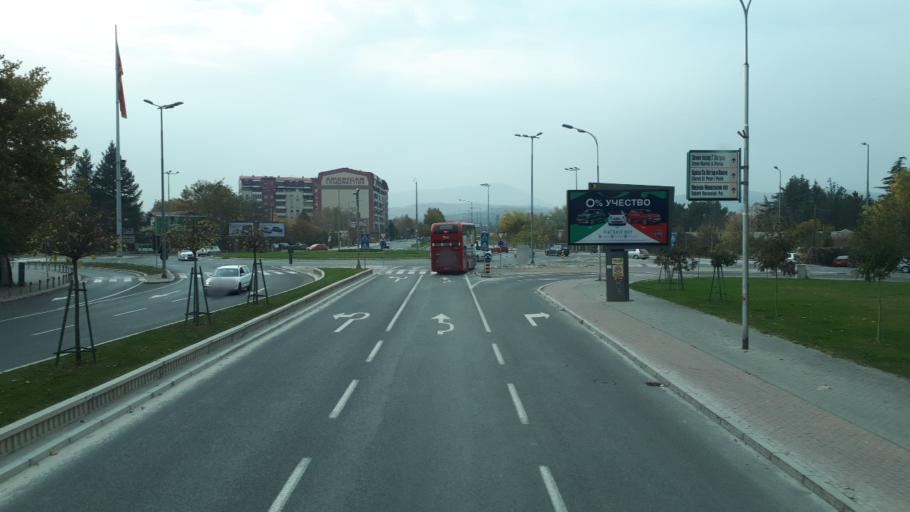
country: MK
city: Krushopek
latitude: 42.0084
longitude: 21.3694
